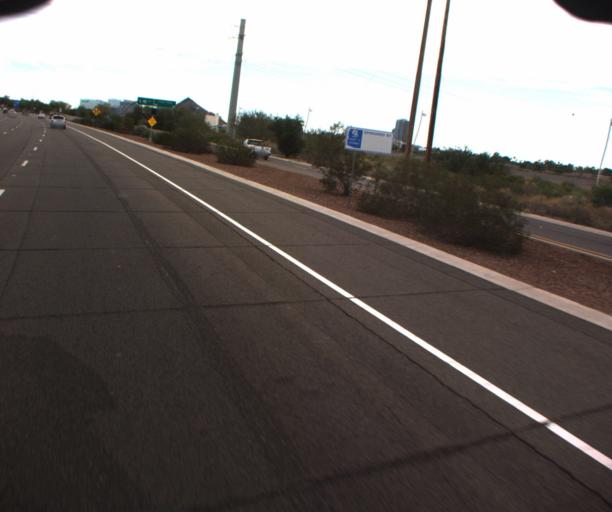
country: US
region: Arizona
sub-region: Maricopa County
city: Tempe Junction
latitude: 33.4367
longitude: -111.9573
